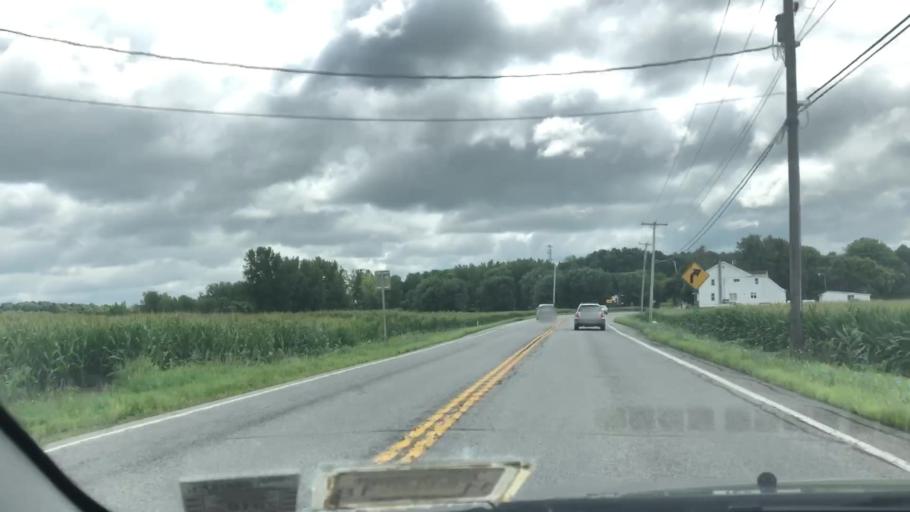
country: US
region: New York
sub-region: Wayne County
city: Macedon
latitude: 43.0986
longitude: -77.2942
